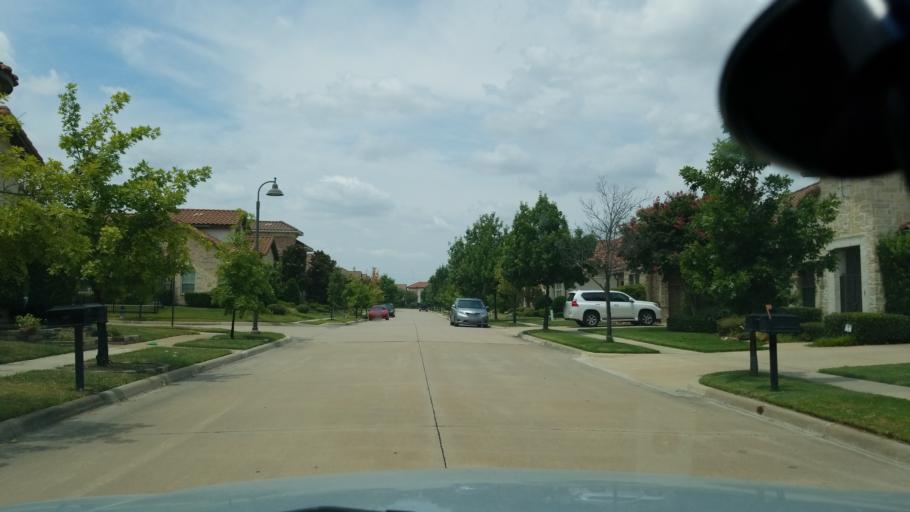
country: US
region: Texas
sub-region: Dallas County
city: Farmers Branch
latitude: 32.9047
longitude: -96.9330
